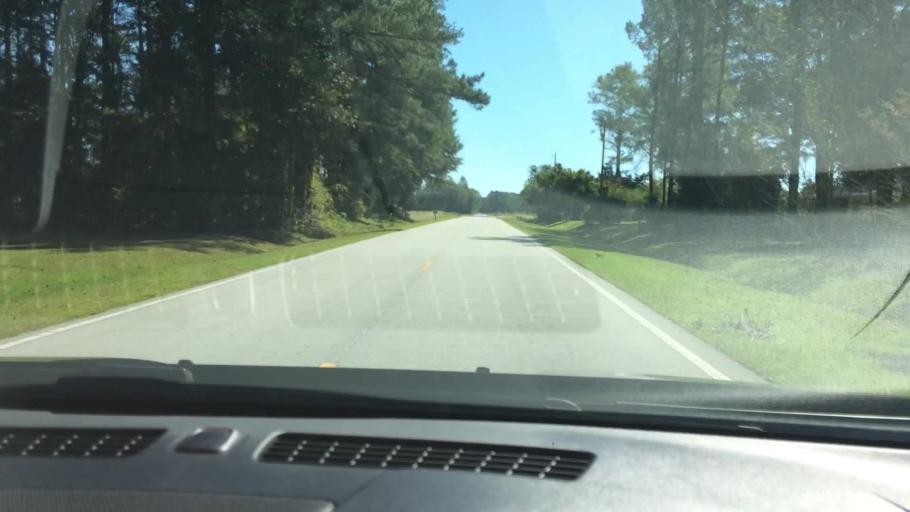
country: US
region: North Carolina
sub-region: Pitt County
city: Grifton
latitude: 35.3402
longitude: -77.3120
